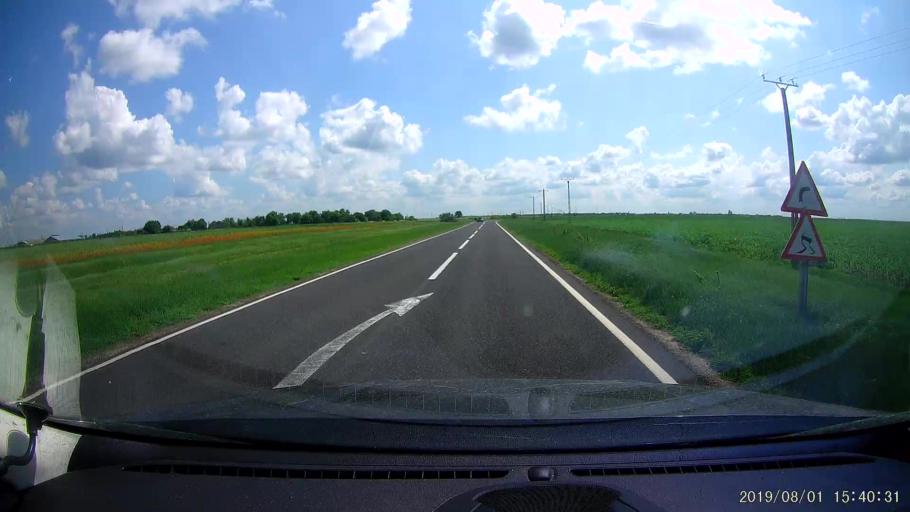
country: RO
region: Braila
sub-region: Comuna Baraganul
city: Baraganul
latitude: 44.8360
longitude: 27.5414
